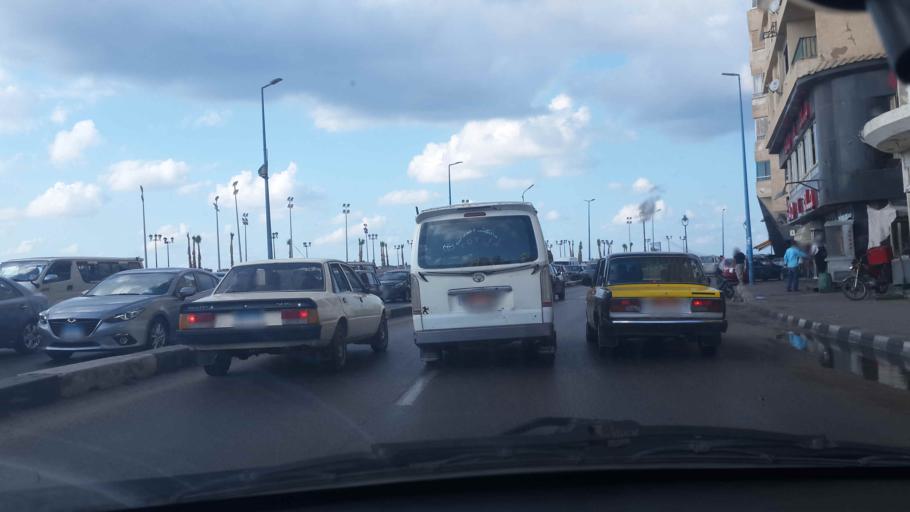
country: EG
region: Alexandria
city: Alexandria
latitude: 31.2680
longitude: 29.9870
